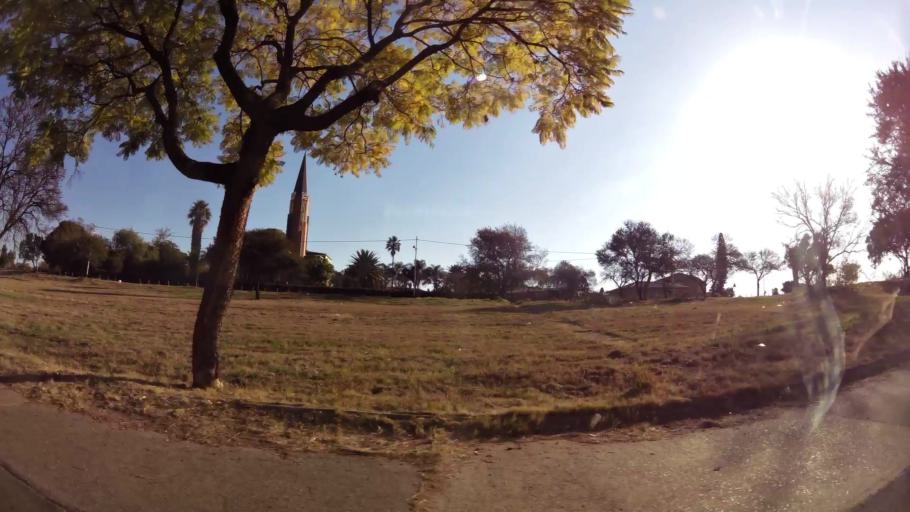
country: ZA
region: Gauteng
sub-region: City of Tshwane Metropolitan Municipality
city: Pretoria
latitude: -25.7523
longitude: 28.1331
